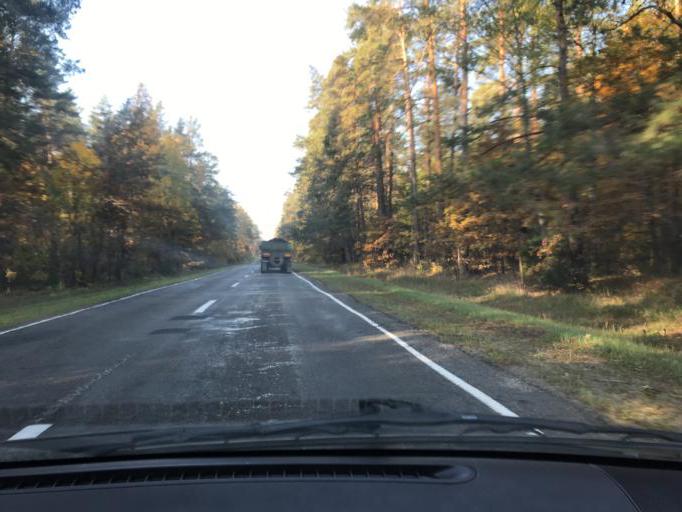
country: BY
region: Brest
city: Tsyelyakhany
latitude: 52.8700
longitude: 25.7135
